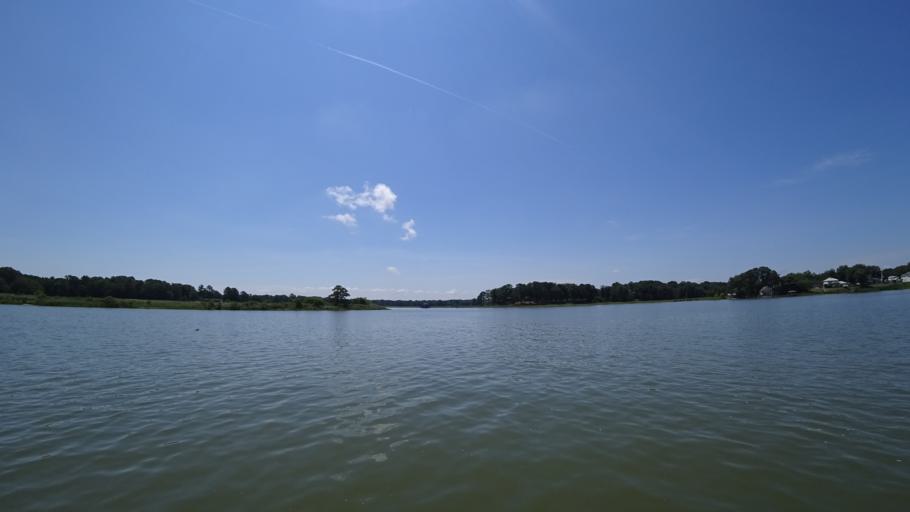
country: US
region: Virginia
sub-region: Isle of Wight County
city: Carrollton
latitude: 37.0014
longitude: -76.5718
